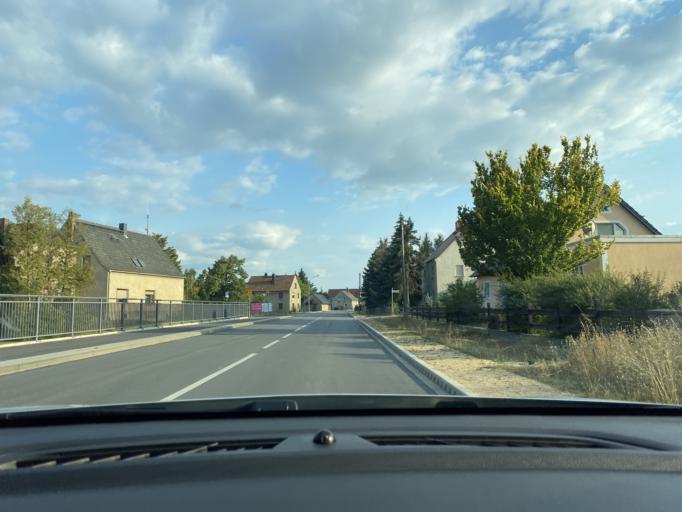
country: DE
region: Saxony
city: Konigswartha
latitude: 51.3304
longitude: 14.3418
